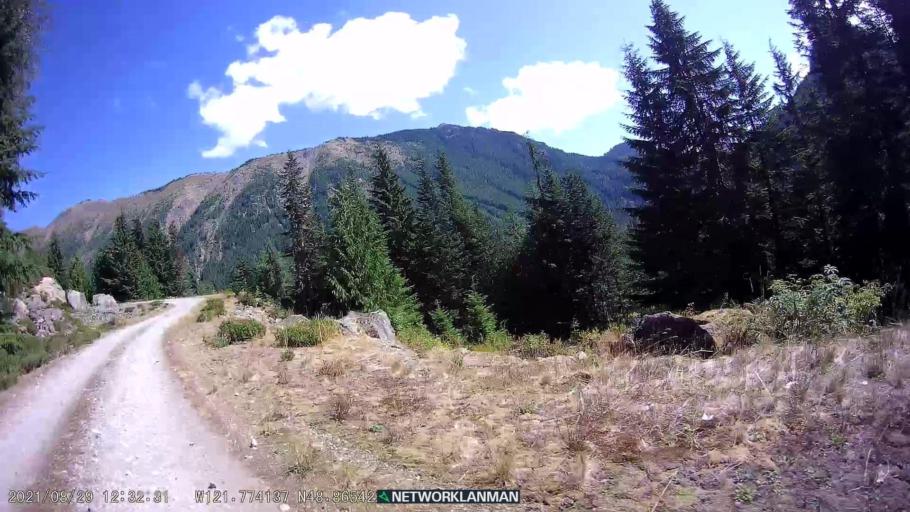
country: CA
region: British Columbia
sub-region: Fraser Valley Regional District
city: Chilliwack
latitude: 48.8655
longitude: -121.7742
